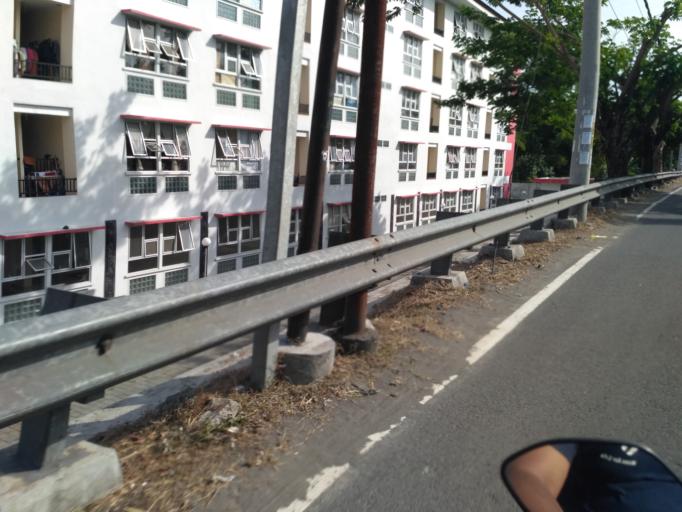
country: ID
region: Daerah Istimewa Yogyakarta
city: Sewon
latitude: -7.8366
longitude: 110.3773
